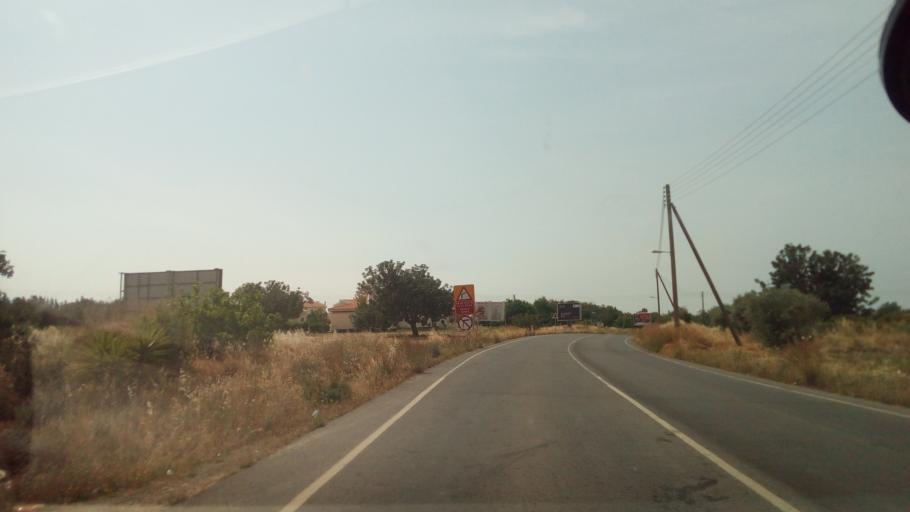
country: CY
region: Pafos
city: Empa
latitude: 34.8075
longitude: 32.4314
